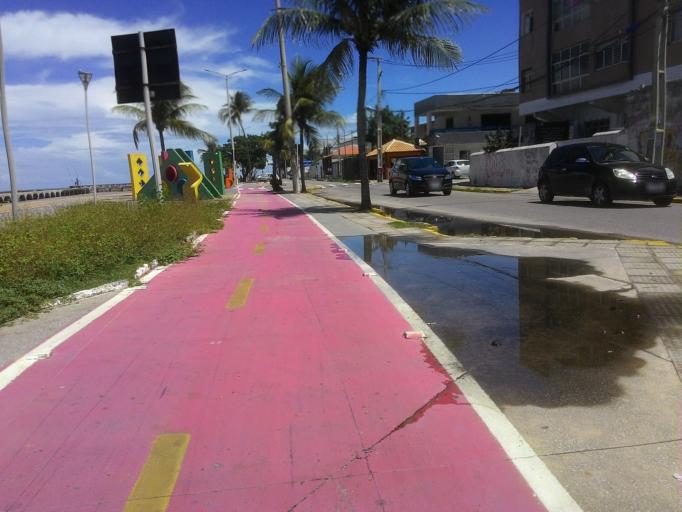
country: BR
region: Pernambuco
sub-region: Olinda
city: Olinda
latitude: -8.0019
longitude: -34.8394
